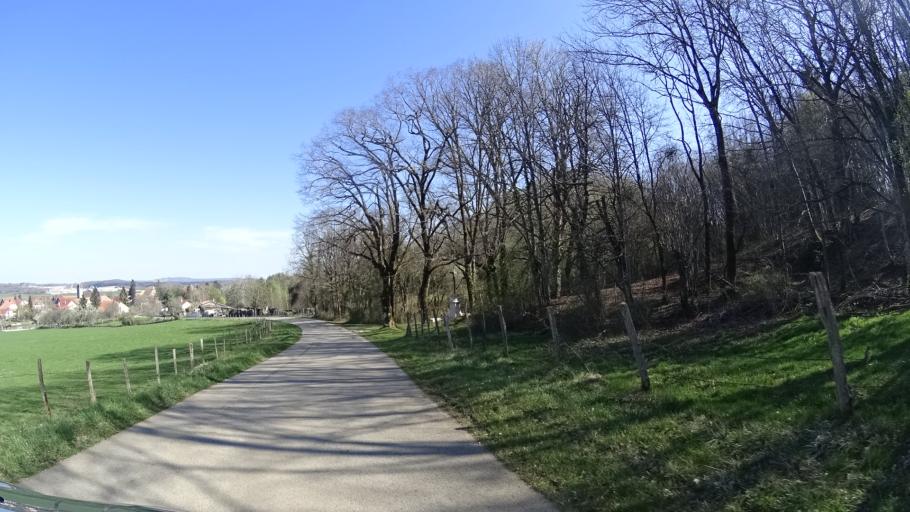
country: FR
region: Franche-Comte
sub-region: Departement du Doubs
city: Ornans
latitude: 47.1407
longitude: 6.0903
